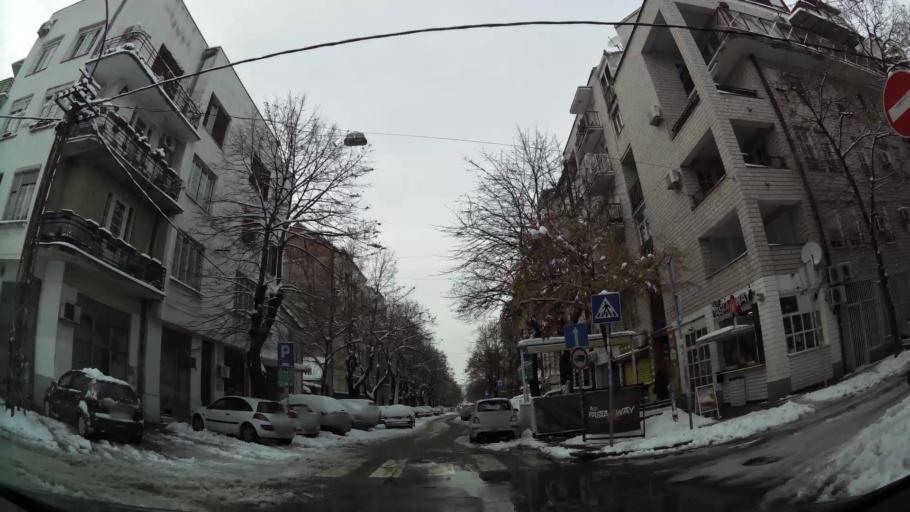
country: RS
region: Central Serbia
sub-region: Belgrade
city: Stari Grad
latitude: 44.8203
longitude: 20.4691
